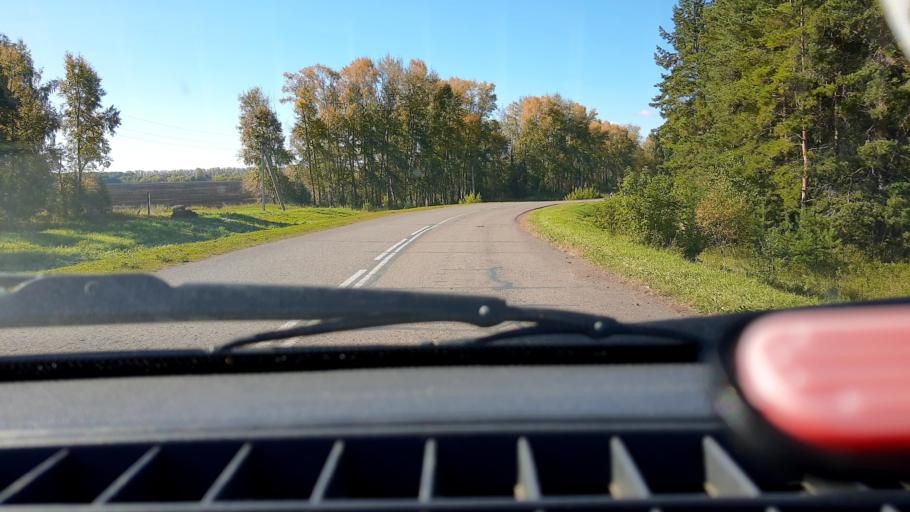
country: RU
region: Bashkortostan
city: Kushnarenkovo
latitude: 55.0643
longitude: 55.4483
